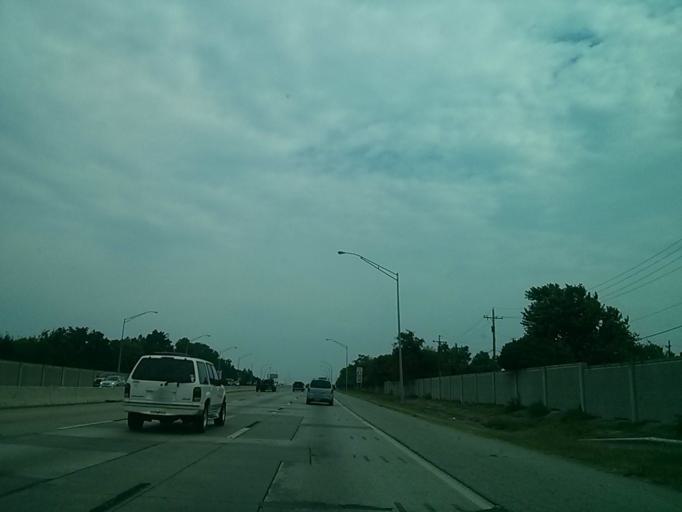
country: US
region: Oklahoma
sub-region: Tulsa County
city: Broken Arrow
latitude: 36.1251
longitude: -95.8596
